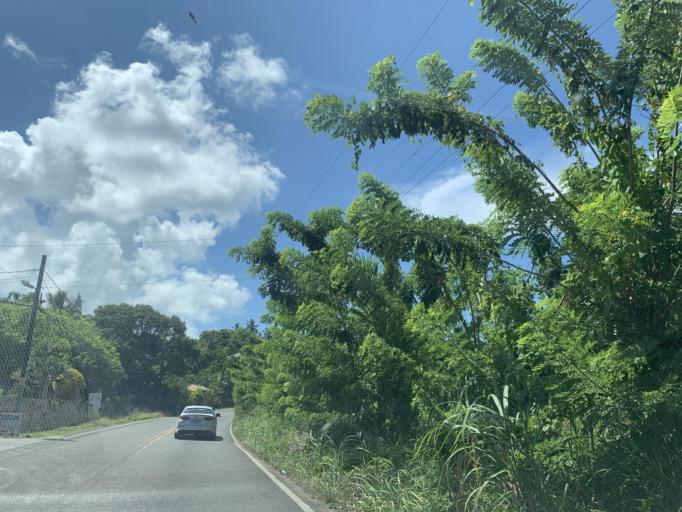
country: DO
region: Maria Trinidad Sanchez
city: Cabrera
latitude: 19.6485
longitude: -69.9270
